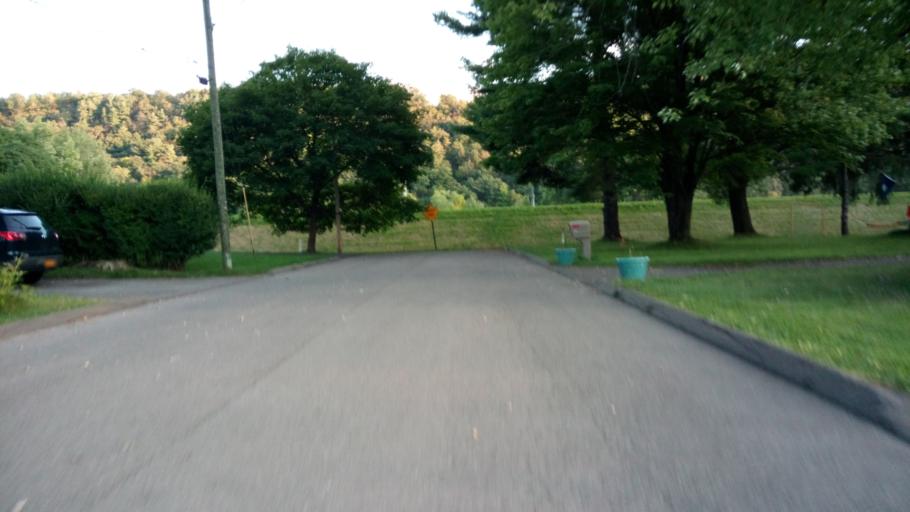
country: US
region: New York
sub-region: Chemung County
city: West Elmira
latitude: 42.0767
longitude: -76.8367
